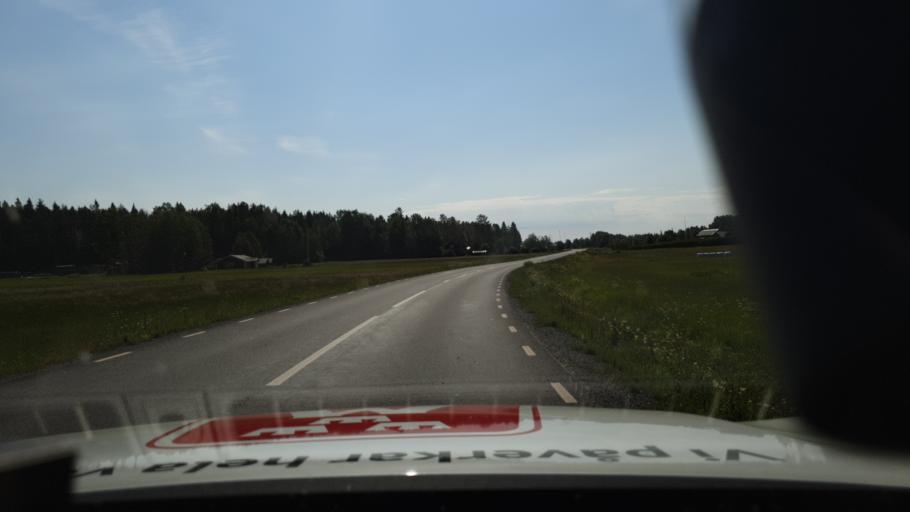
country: SE
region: Norrbotten
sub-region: Lulea Kommun
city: Sodra Sunderbyn
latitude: 65.8182
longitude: 21.9990
